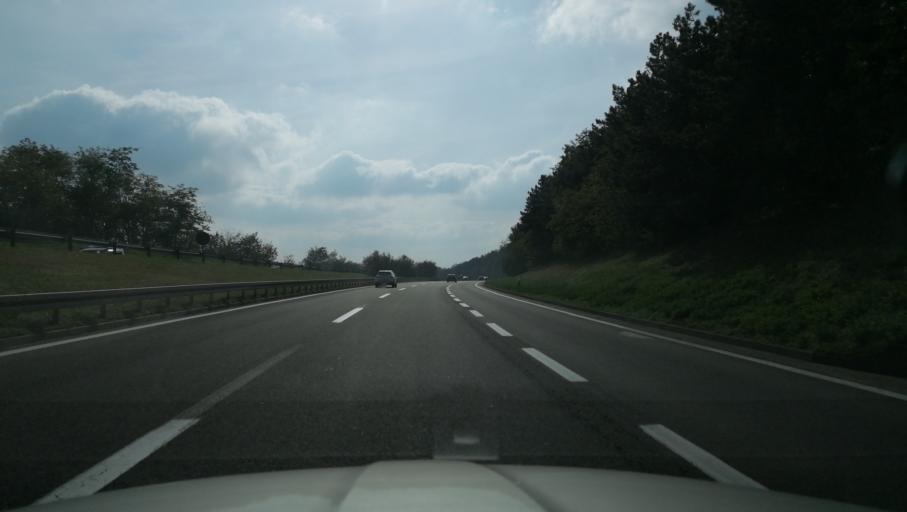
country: RS
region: Central Serbia
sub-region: Belgrade
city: Grocka
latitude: 44.6309
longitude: 20.6377
